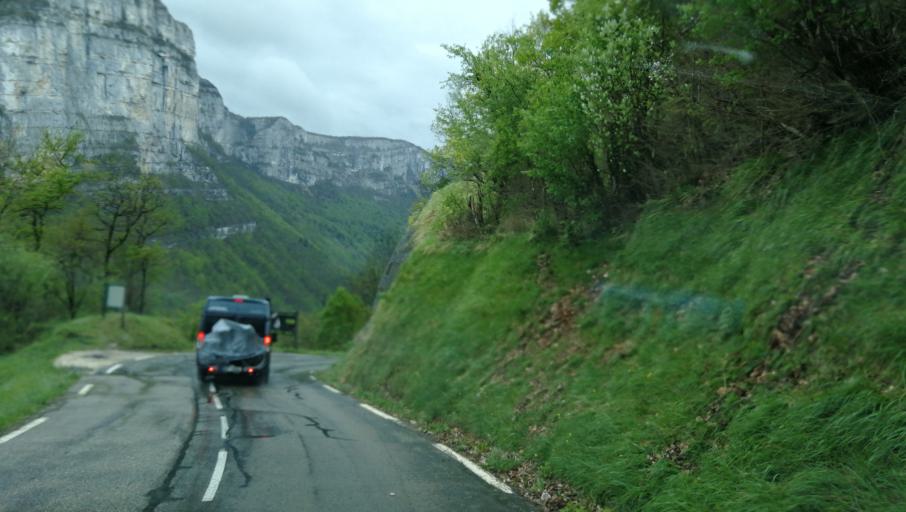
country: FR
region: Rhone-Alpes
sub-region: Departement de l'Isere
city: Pont-en-Royans
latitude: 45.0672
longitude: 5.4310
